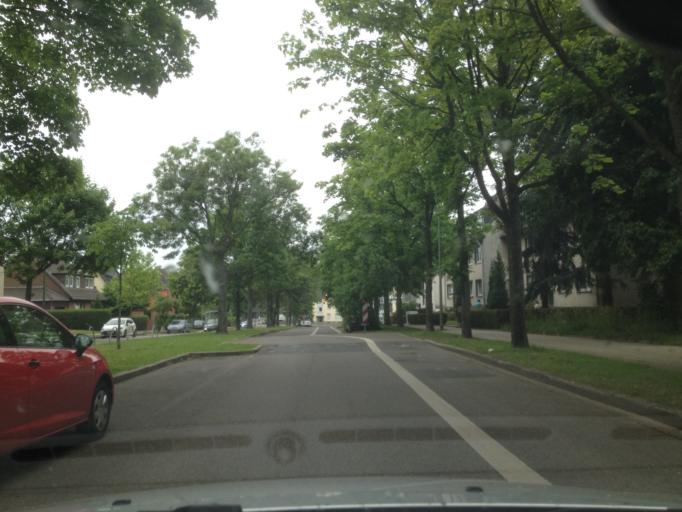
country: DE
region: North Rhine-Westphalia
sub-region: Regierungsbezirk Munster
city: Gelsenkirchen
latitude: 51.4358
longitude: 7.1085
